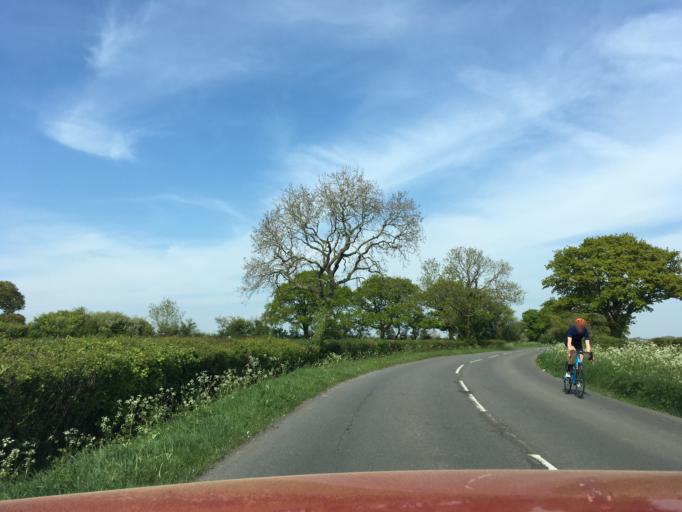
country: GB
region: England
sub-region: South Gloucestershire
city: Chipping Sodbury
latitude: 51.5170
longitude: -2.4039
